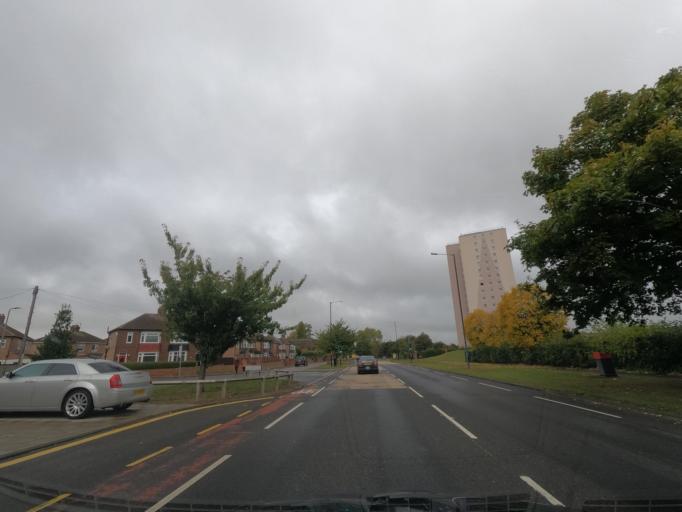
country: GB
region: England
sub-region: Middlesbrough
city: Nunthorpe
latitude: 54.5609
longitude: -1.1901
